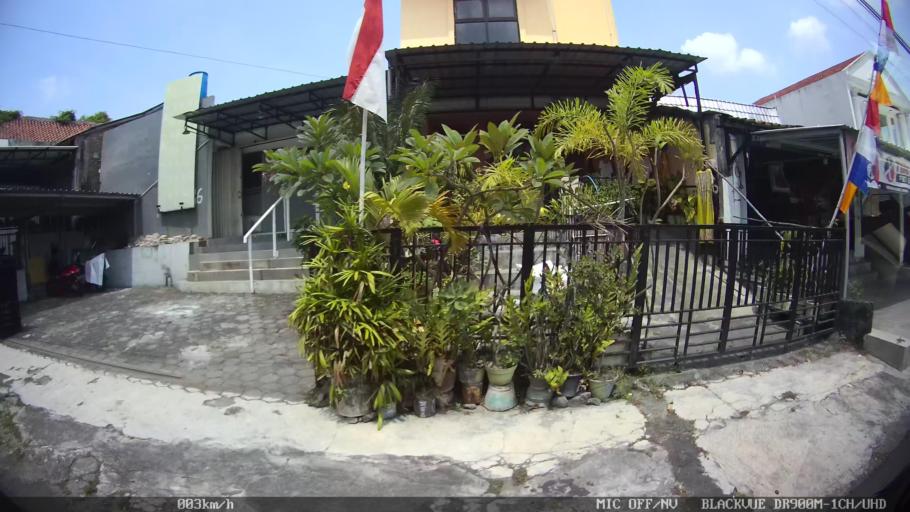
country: ID
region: Daerah Istimewa Yogyakarta
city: Yogyakarta
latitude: -7.8136
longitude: 110.3944
